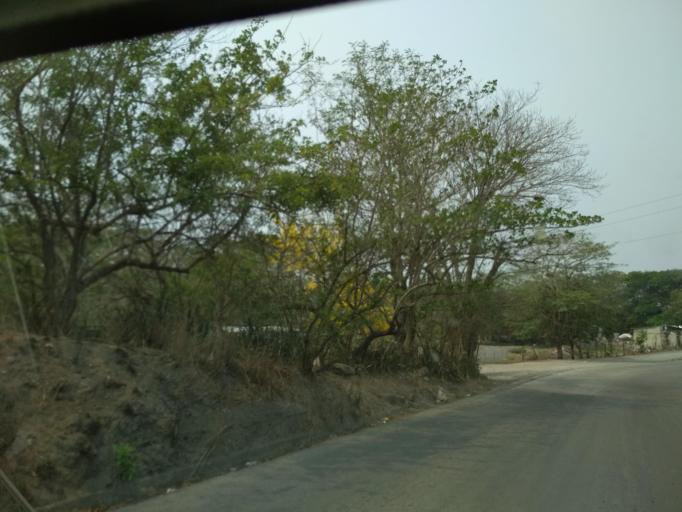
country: MX
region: Veracruz
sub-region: Veracruz
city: Delfino Victoria (Santa Fe)
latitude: 19.1896
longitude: -96.3089
